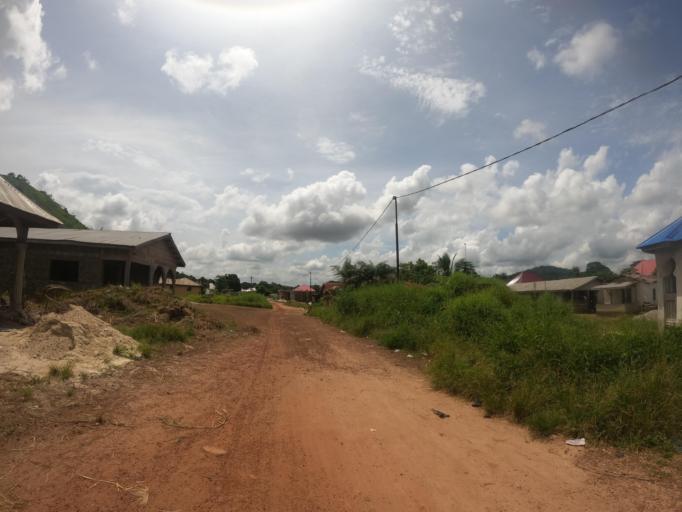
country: SL
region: Northern Province
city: Makeni
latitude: 8.9030
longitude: -12.0581
